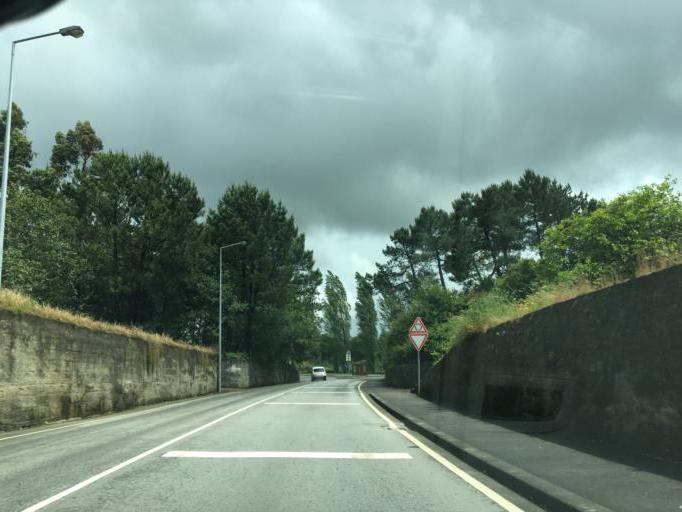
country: PT
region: Porto
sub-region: Maia
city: Nogueira
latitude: 41.2592
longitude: -8.6013
